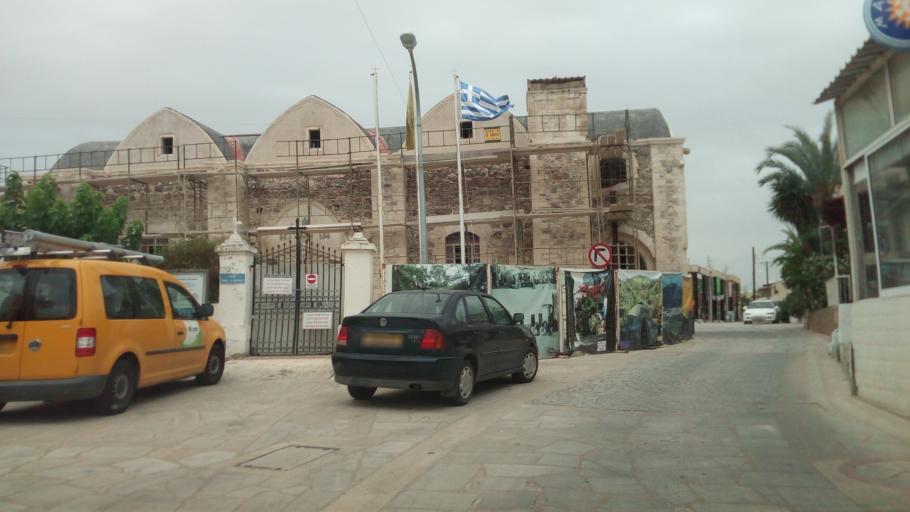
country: CY
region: Larnaka
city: Kornos
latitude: 34.9229
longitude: 33.3968
